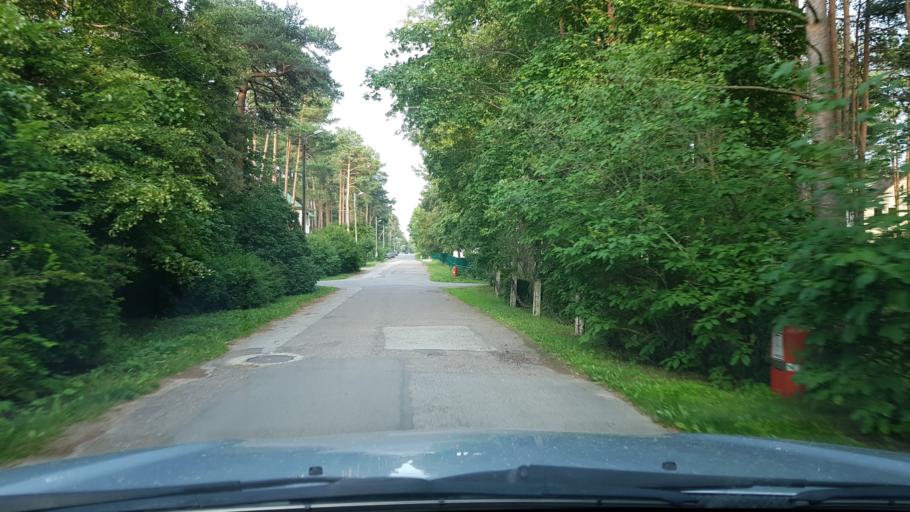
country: EE
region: Ida-Virumaa
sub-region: Narva-Joesuu linn
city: Narva-Joesuu
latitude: 59.4568
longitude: 28.0443
